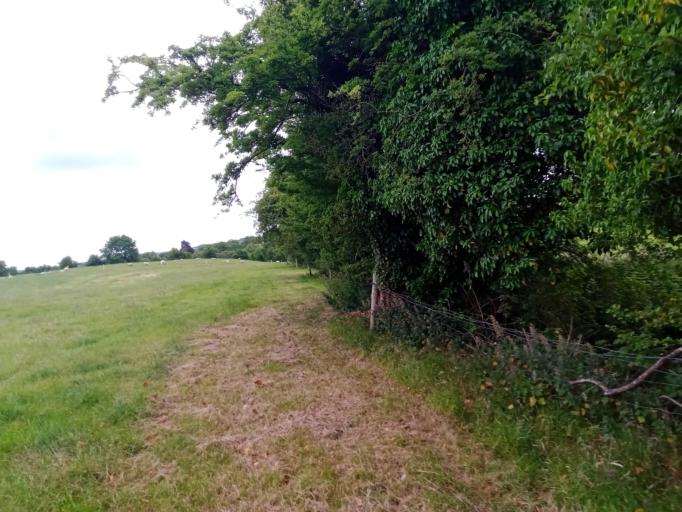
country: IE
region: Leinster
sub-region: Laois
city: Rathdowney
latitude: 52.7812
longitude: -7.4670
